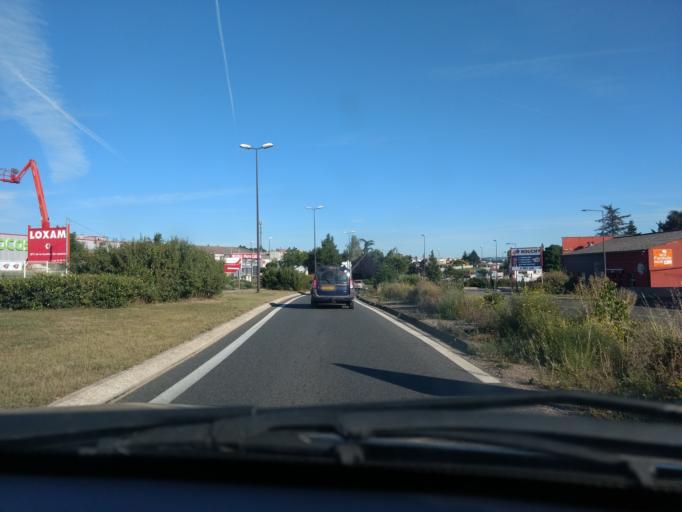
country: FR
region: Midi-Pyrenees
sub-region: Departement de l'Aveyron
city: Olemps
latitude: 44.3742
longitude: 2.5448
